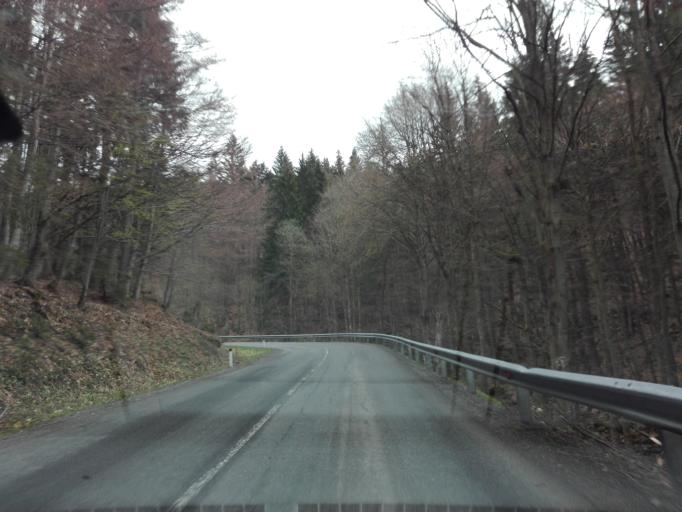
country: AT
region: Upper Austria
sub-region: Politischer Bezirk Rohrbach
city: Ulrichsberg
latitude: 48.7316
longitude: 13.8936
